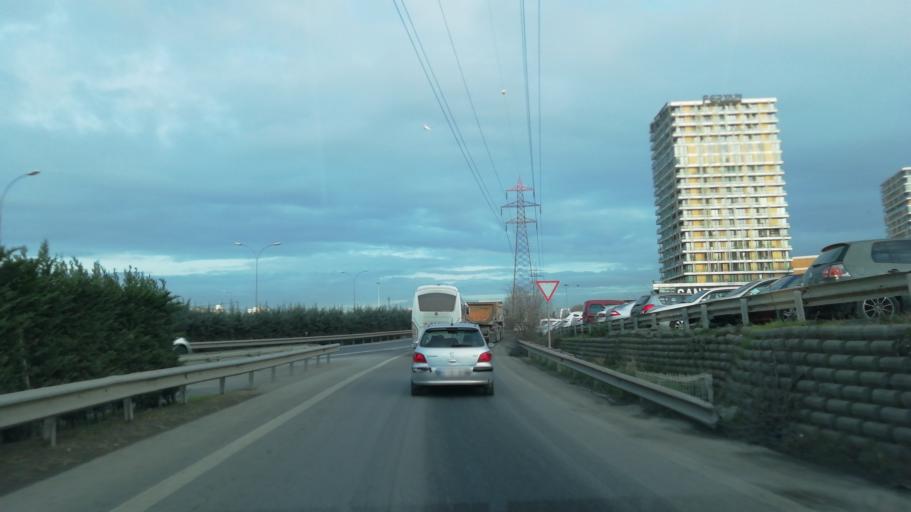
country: TR
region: Istanbul
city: Bahcelievler
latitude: 41.0058
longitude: 28.8144
